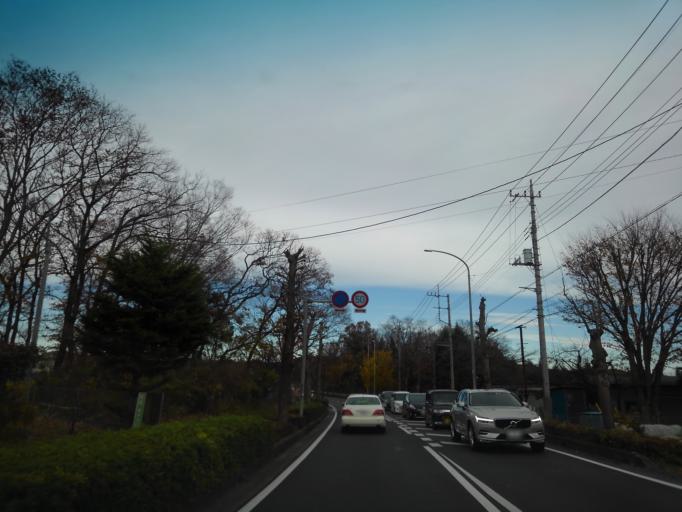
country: JP
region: Saitama
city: Morohongo
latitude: 35.9521
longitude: 139.3142
